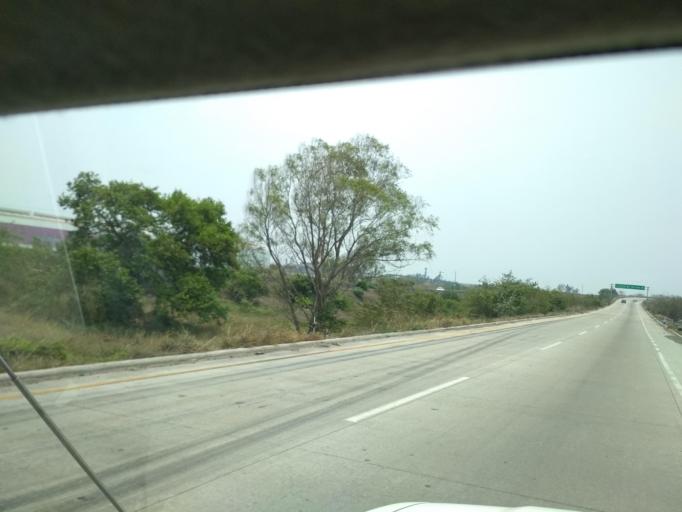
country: MX
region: Veracruz
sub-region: Veracruz
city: Oasis
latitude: 19.1891
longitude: -96.2460
